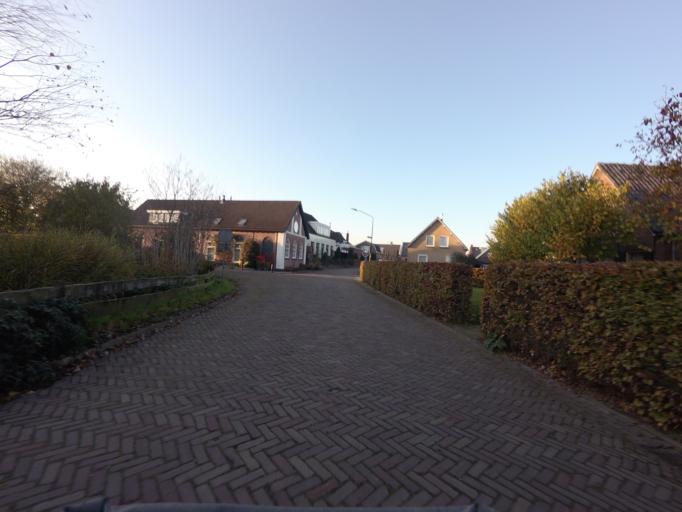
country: NL
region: North Brabant
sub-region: Gemeente Woudrichem
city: Woudrichem
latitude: 51.7909
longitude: 5.0351
